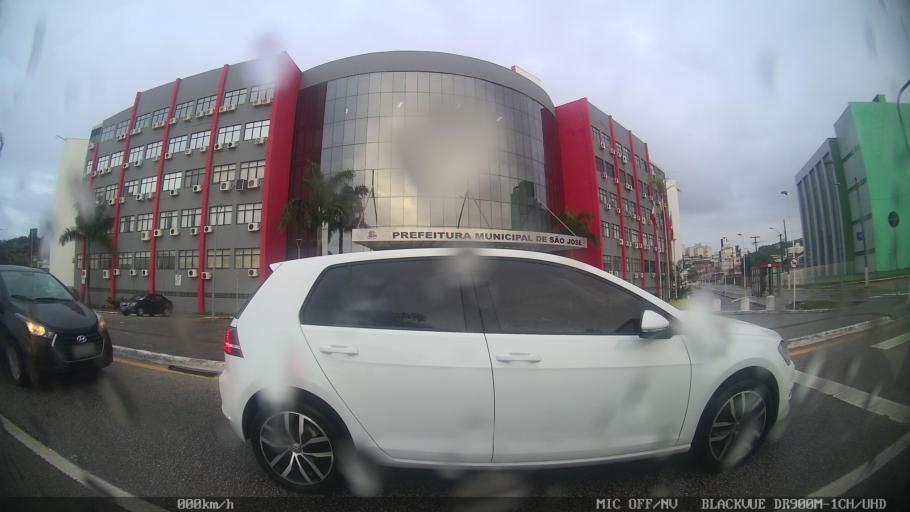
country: BR
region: Santa Catarina
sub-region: Sao Jose
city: Campinas
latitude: -27.6092
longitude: -48.6264
